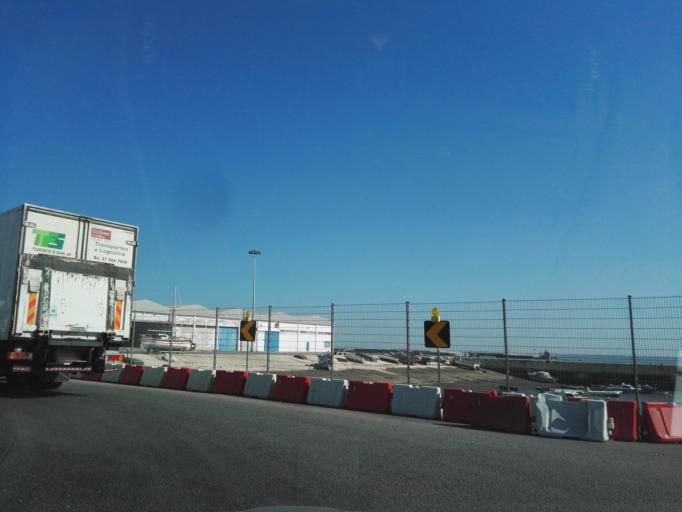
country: PT
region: Lisbon
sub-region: Loures
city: Moscavide
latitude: 38.7416
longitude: -9.0999
